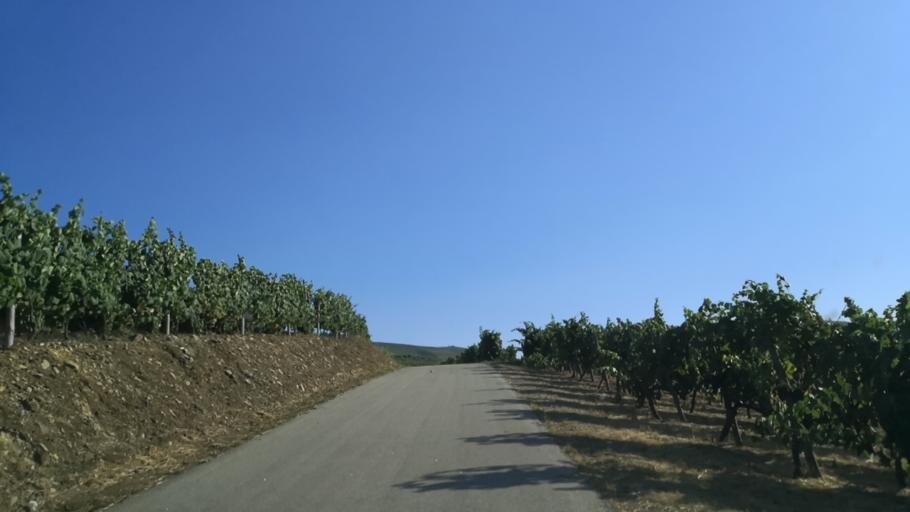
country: PT
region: Viseu
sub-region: Sao Joao da Pesqueira
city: Sao Joao da Pesqueira
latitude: 41.1836
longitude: -7.4021
